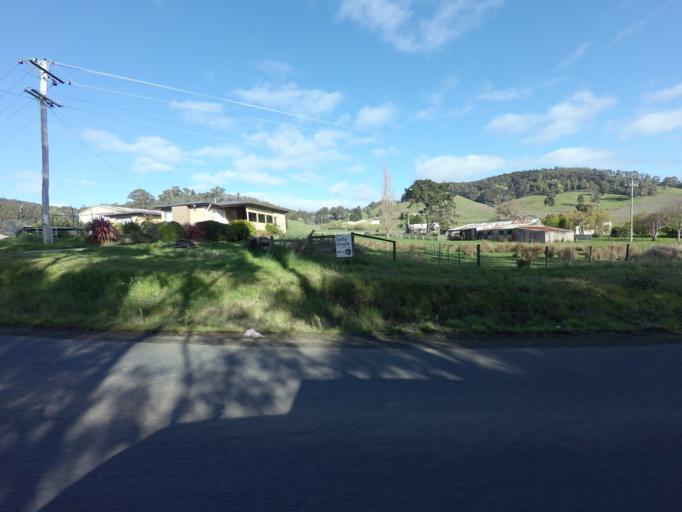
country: AU
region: Tasmania
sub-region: Huon Valley
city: Geeveston
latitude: -43.1905
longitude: 146.9599
